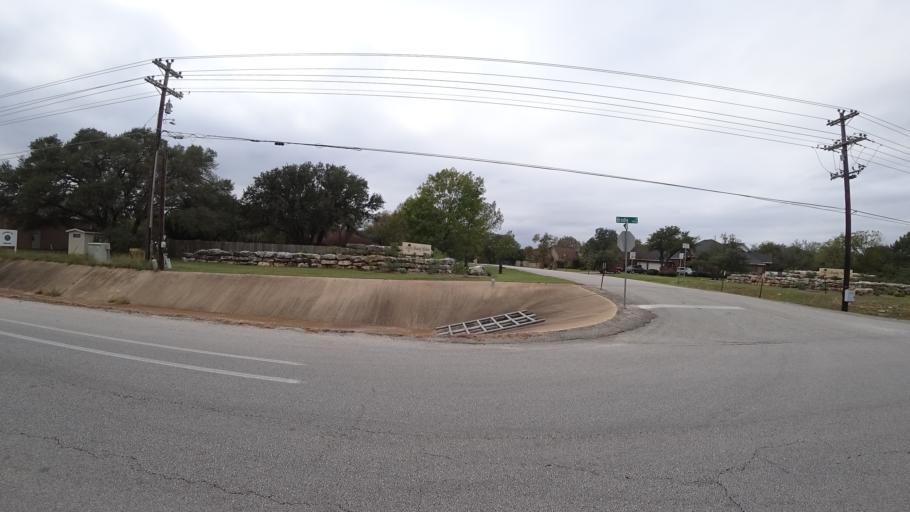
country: US
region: Texas
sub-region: Travis County
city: Shady Hollow
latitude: 30.1582
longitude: -97.8599
